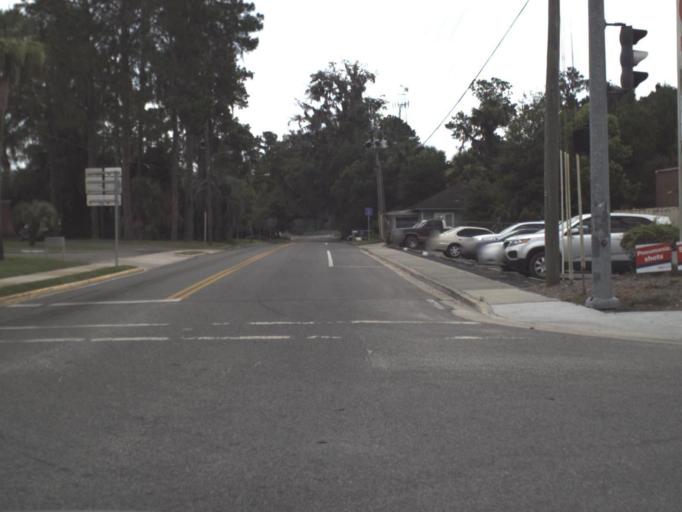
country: US
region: Florida
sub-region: Hamilton County
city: Jasper
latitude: 30.5180
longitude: -82.9458
